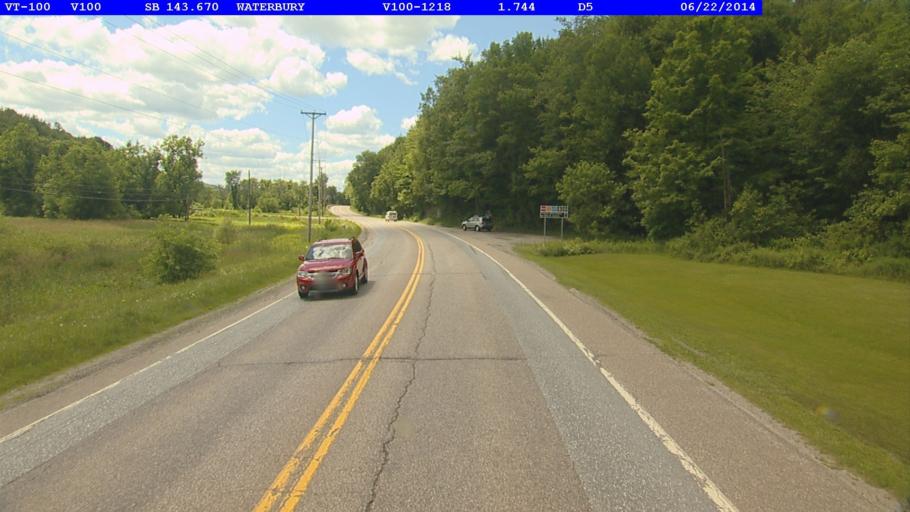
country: US
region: Vermont
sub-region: Washington County
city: Waterbury
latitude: 44.3570
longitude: -72.7349
